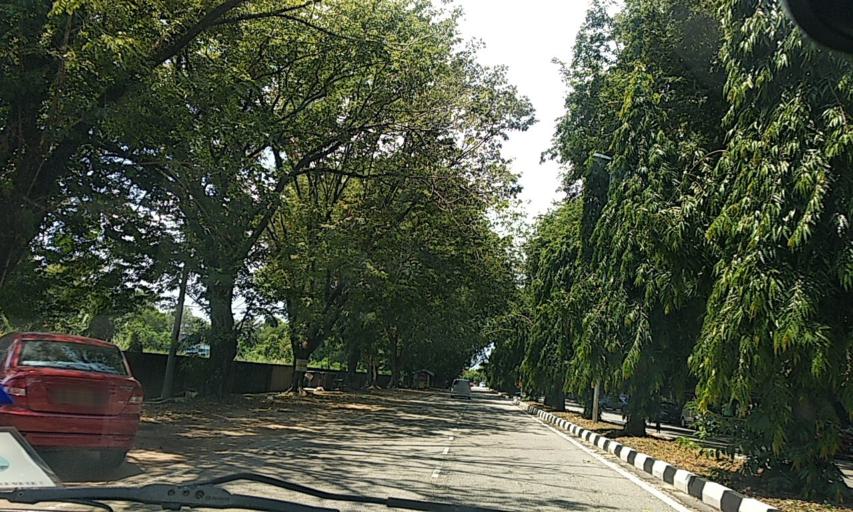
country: MY
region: Kedah
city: Sungai Petani
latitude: 5.6353
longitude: 100.4773
